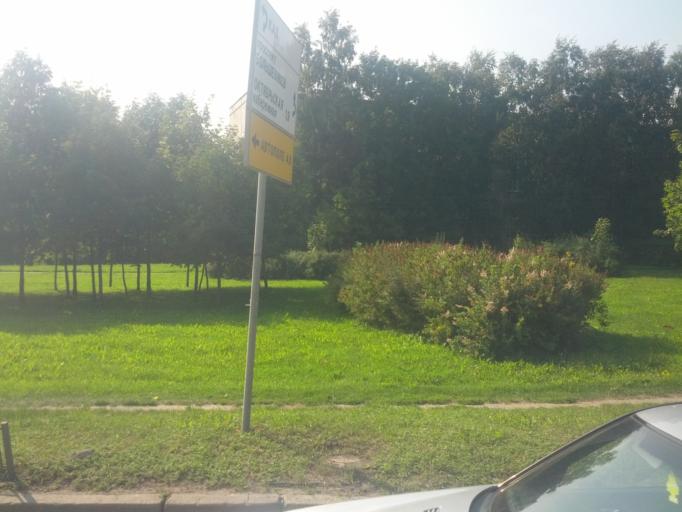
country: RU
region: Leningrad
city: Rybatskoye
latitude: 59.8870
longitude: 30.4894
